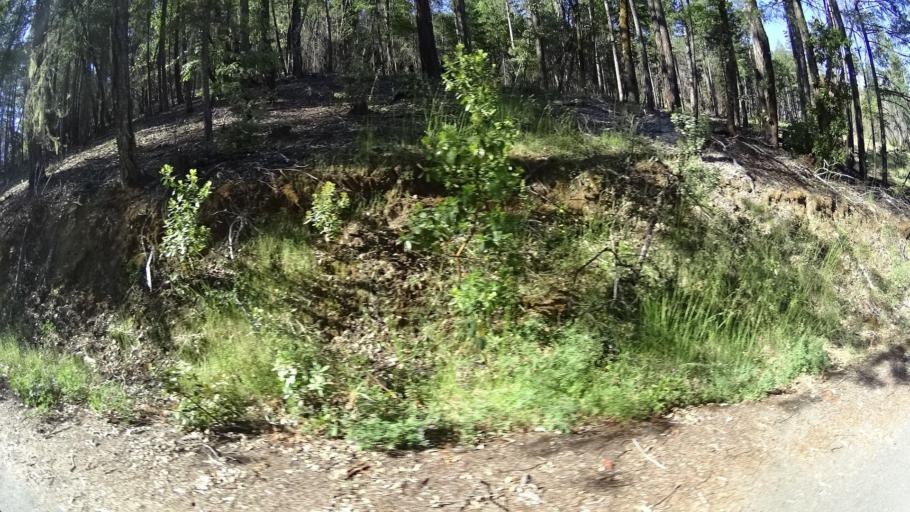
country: US
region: California
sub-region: Lake County
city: Upper Lake
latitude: 39.4020
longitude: -122.9599
